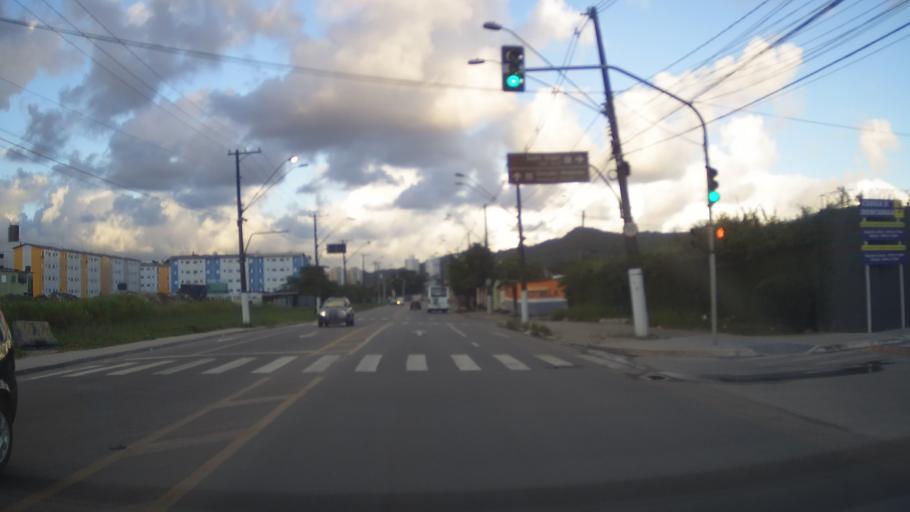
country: BR
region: Sao Paulo
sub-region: Sao Vicente
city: Sao Vicente
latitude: -23.9502
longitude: -46.3892
